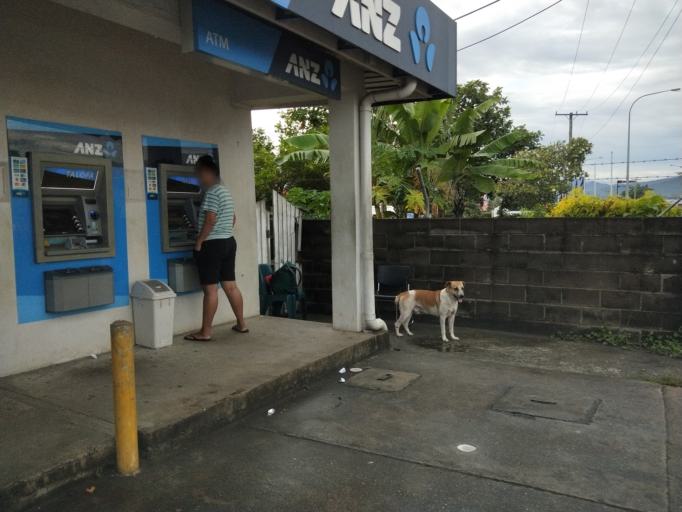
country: WS
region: Tuamasaga
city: Vaiusu
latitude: -13.8193
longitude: -171.8055
